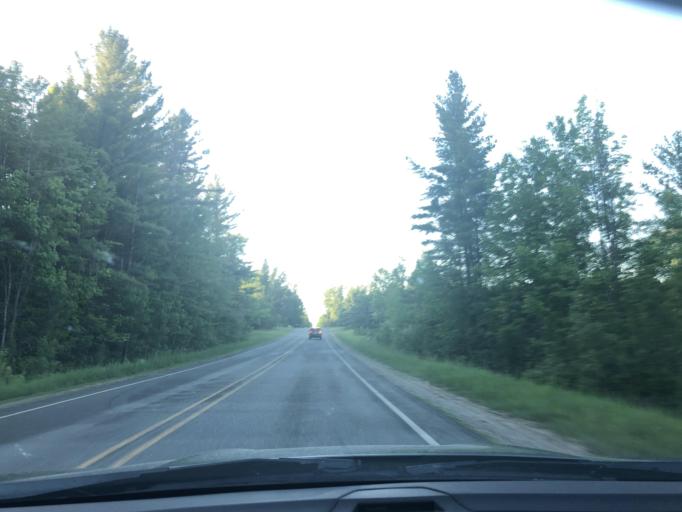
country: US
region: Michigan
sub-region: Missaukee County
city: Lake City
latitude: 44.4480
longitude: -85.0748
